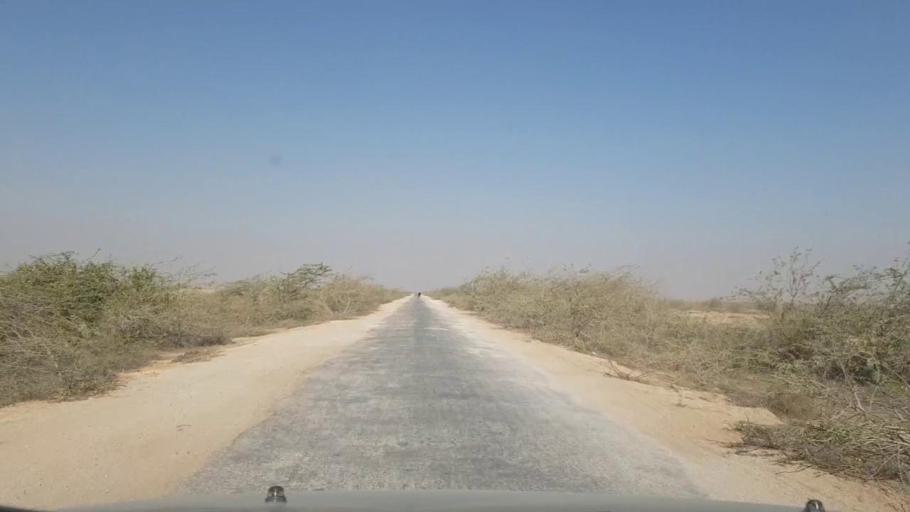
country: PK
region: Sindh
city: Thatta
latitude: 24.8338
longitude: 67.8906
